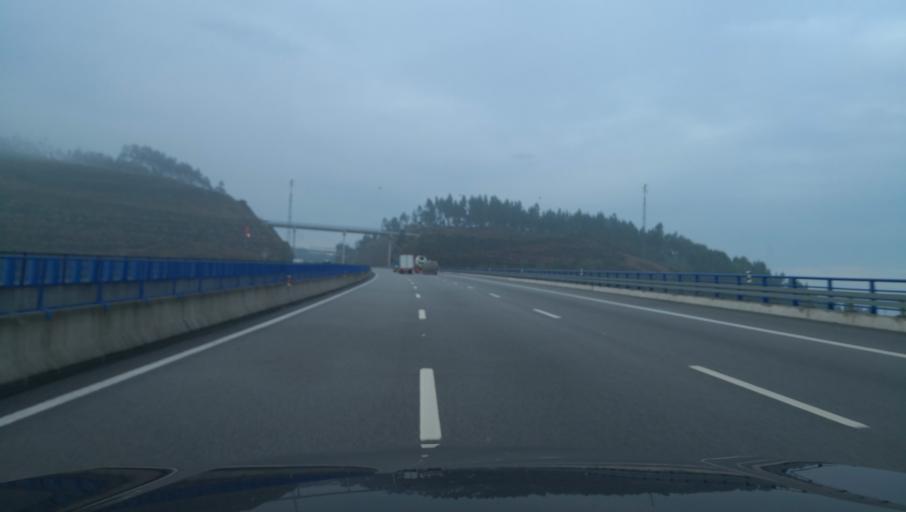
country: PT
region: Porto
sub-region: Paredes
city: Recarei
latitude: 41.1283
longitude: -8.4311
